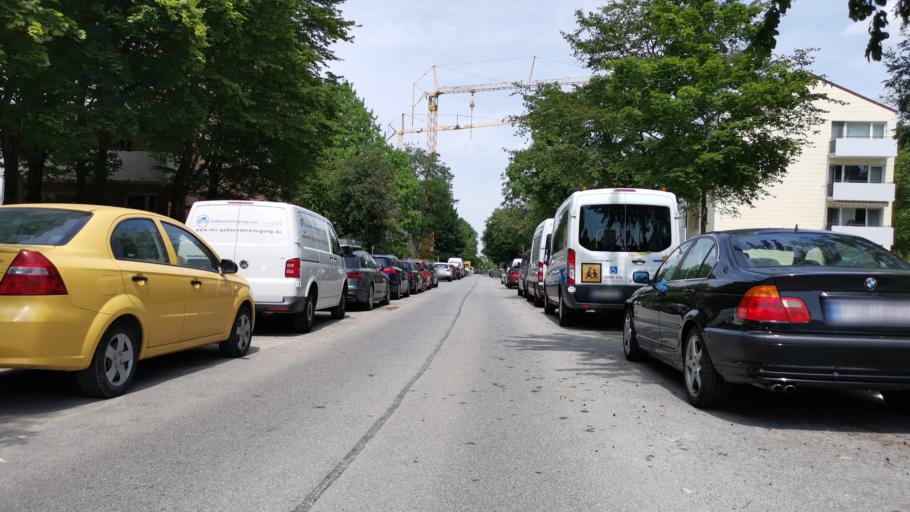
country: DE
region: Bavaria
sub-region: Upper Bavaria
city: Neuried
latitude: 48.0796
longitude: 11.4860
